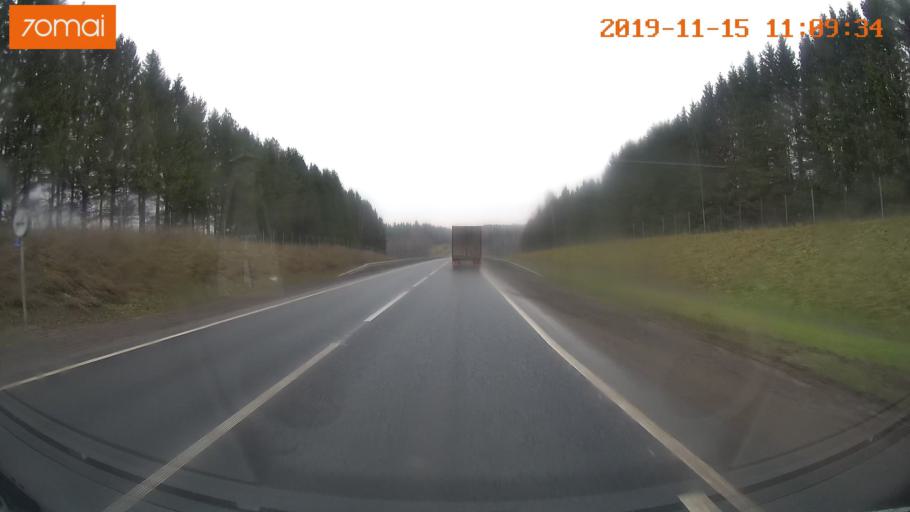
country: RU
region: Vologda
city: Chebsara
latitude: 59.1205
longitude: 39.1009
